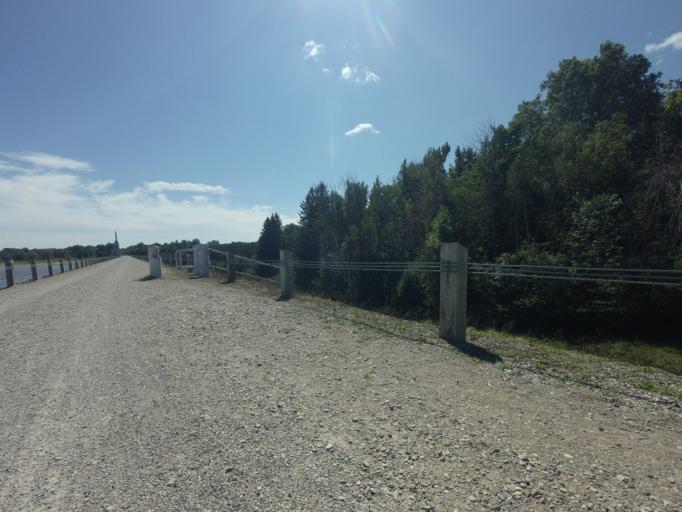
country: CA
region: Ontario
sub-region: Wellington County
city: Guelph
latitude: 43.7353
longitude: -80.3405
